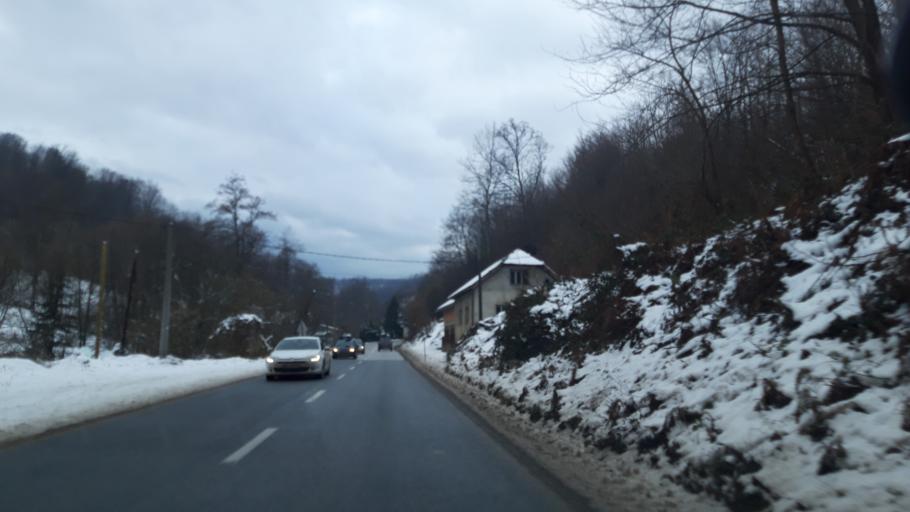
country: BA
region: Republika Srpska
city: Vlasenica
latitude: 44.1849
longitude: 18.9941
